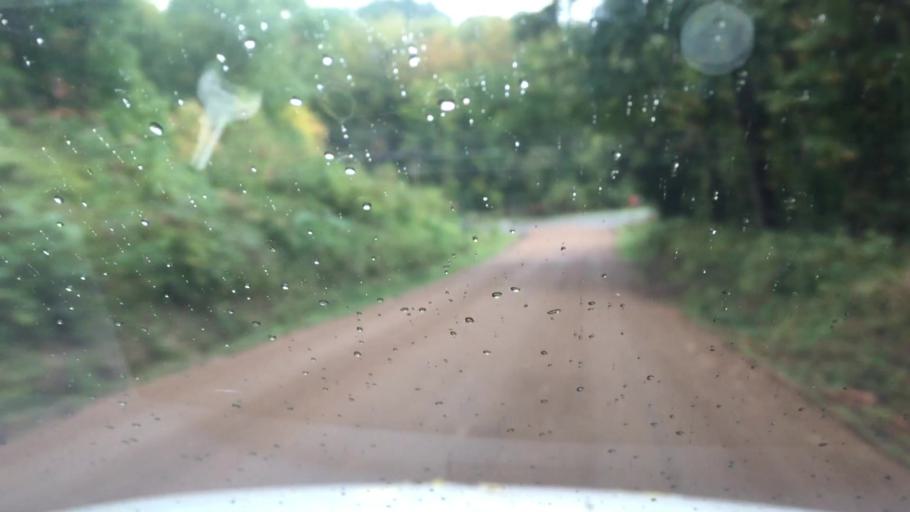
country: US
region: Missouri
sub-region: Boone County
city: Columbia
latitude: 38.8820
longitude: -92.4194
